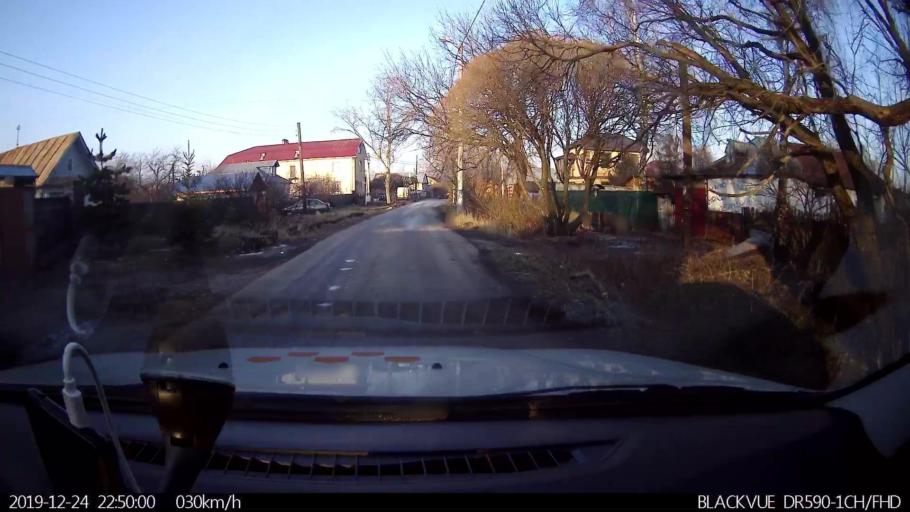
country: RU
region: Nizjnij Novgorod
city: Nizhniy Novgorod
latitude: 56.2886
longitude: 43.8993
